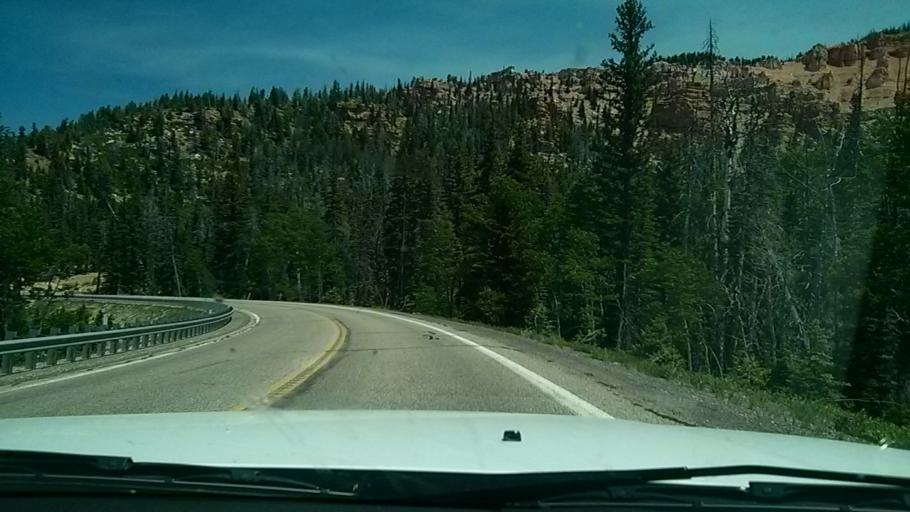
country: US
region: Utah
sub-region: Iron County
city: Cedar City
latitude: 37.5879
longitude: -112.8826
